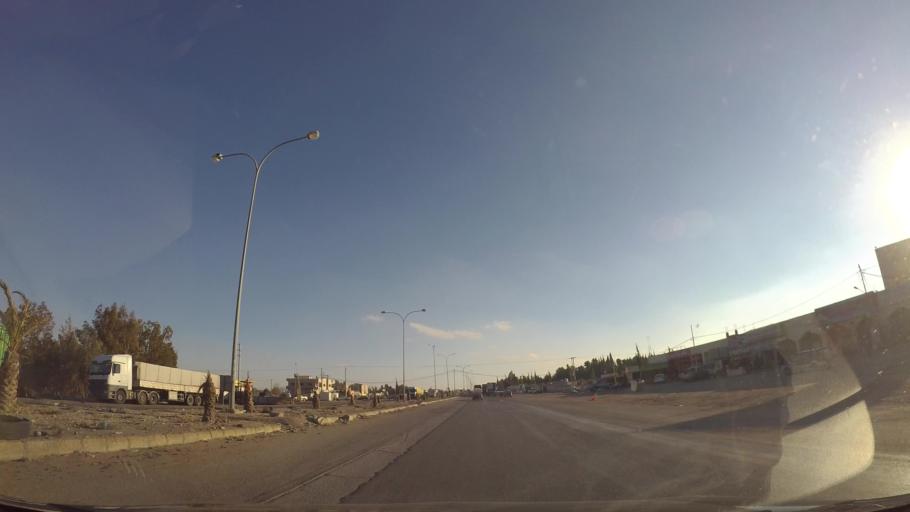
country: JO
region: Tafielah
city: Busayra
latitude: 30.5993
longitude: 35.8047
